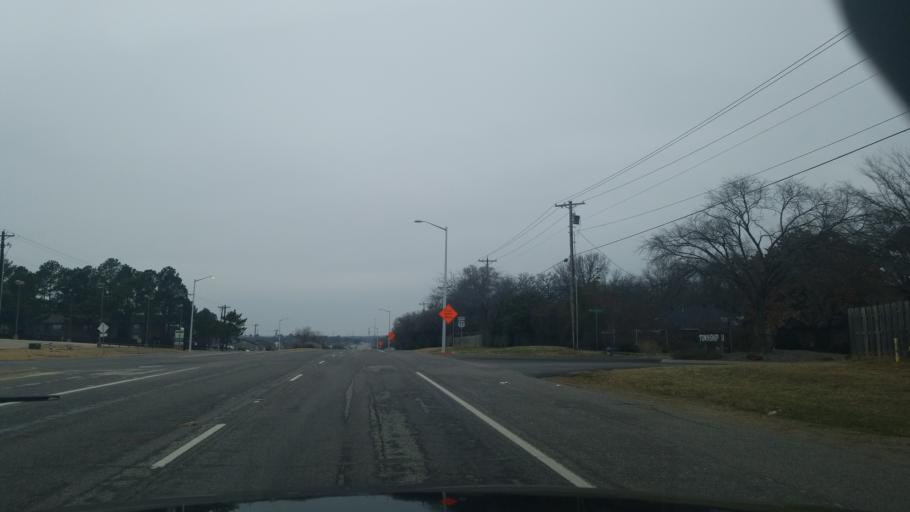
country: US
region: Texas
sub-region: Denton County
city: Denton
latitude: 33.1944
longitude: -97.1178
